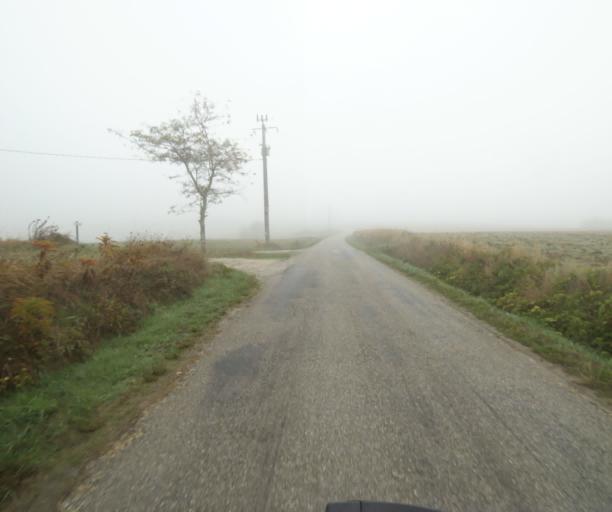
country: FR
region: Midi-Pyrenees
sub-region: Departement de la Haute-Garonne
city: Villemur-sur-Tarn
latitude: 43.9030
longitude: 1.4851
